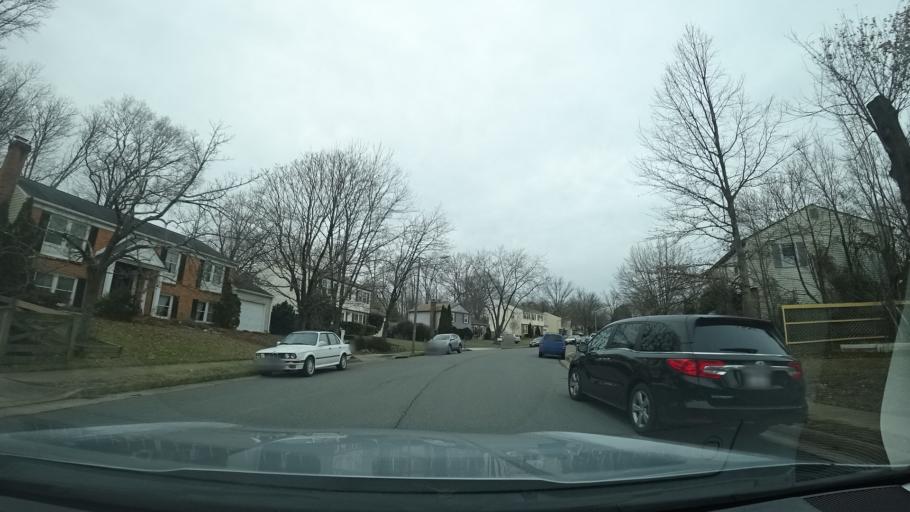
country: US
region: Virginia
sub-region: Fairfax County
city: Herndon
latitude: 38.9767
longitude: -77.3744
